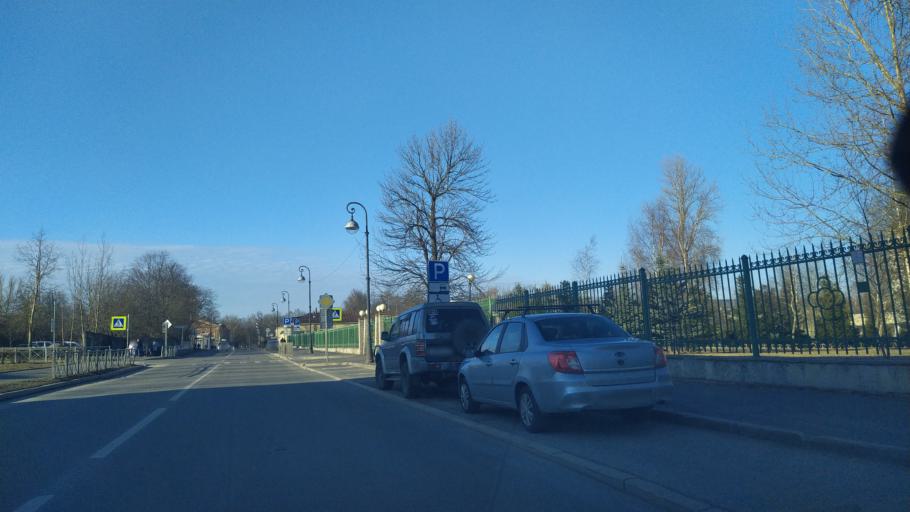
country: RU
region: St.-Petersburg
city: Pushkin
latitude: 59.7048
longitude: 30.3920
